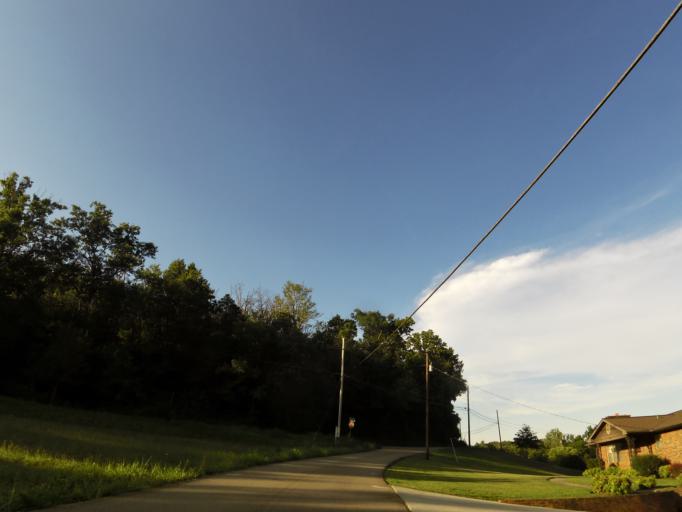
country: US
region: Tennessee
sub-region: Knox County
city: Knoxville
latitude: 35.9076
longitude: -83.9116
